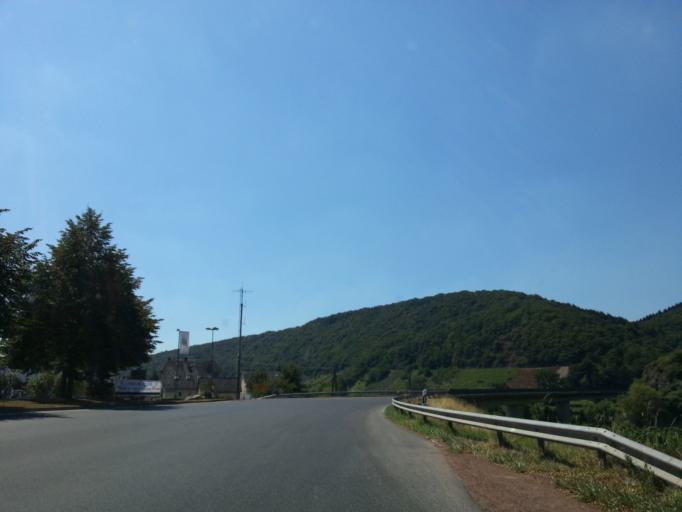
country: DE
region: Rheinland-Pfalz
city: Neumagen-Dhron
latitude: 49.8602
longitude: 6.8981
